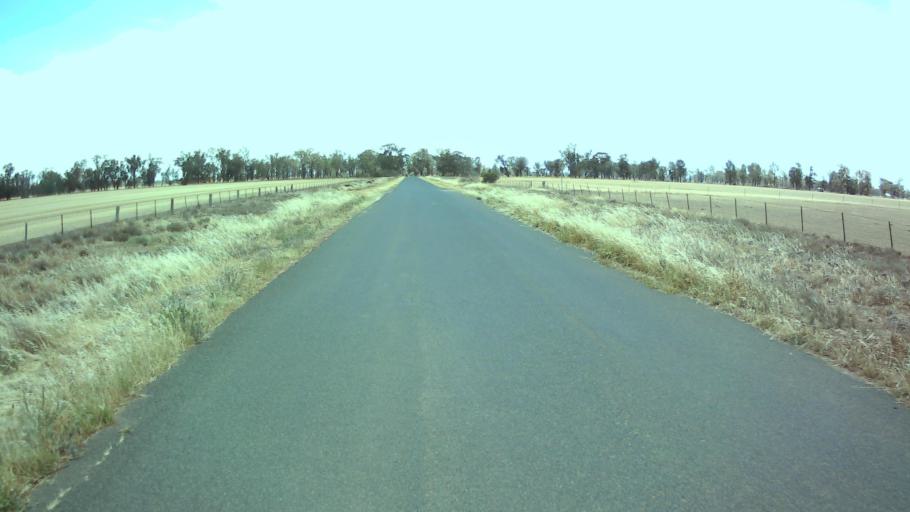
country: AU
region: New South Wales
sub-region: Weddin
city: Grenfell
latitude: -34.0714
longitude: 147.7774
